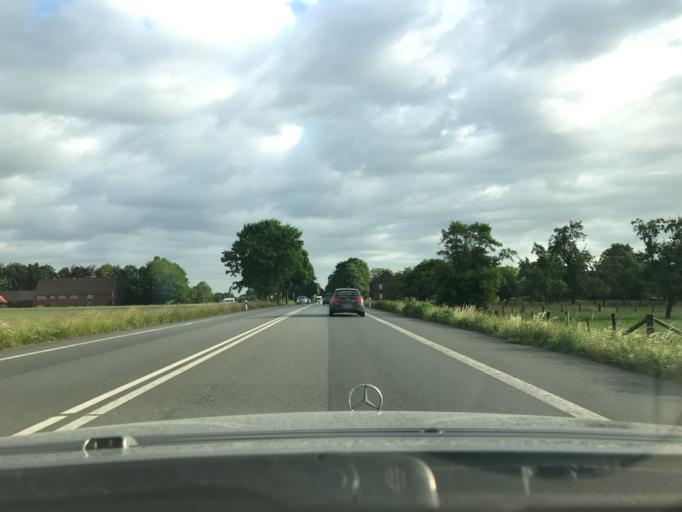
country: DE
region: North Rhine-Westphalia
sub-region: Regierungsbezirk Arnsberg
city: Hamm
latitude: 51.6094
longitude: 7.8519
